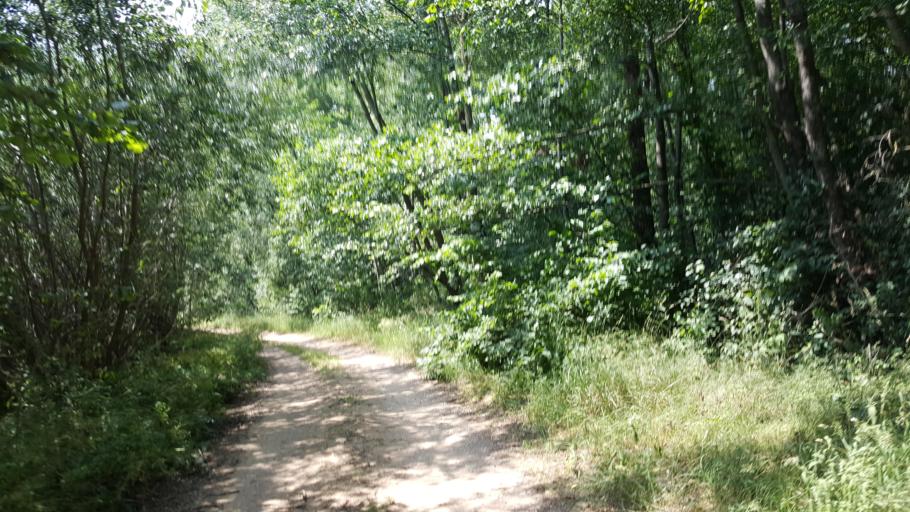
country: BY
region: Brest
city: Kamyanyets
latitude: 52.3656
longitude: 23.7583
